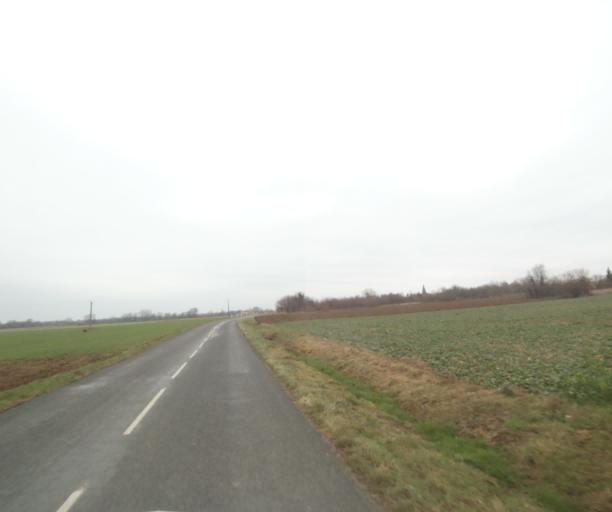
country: FR
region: Champagne-Ardenne
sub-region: Departement de la Haute-Marne
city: Villiers-en-Lieu
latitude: 48.6327
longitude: 4.7705
